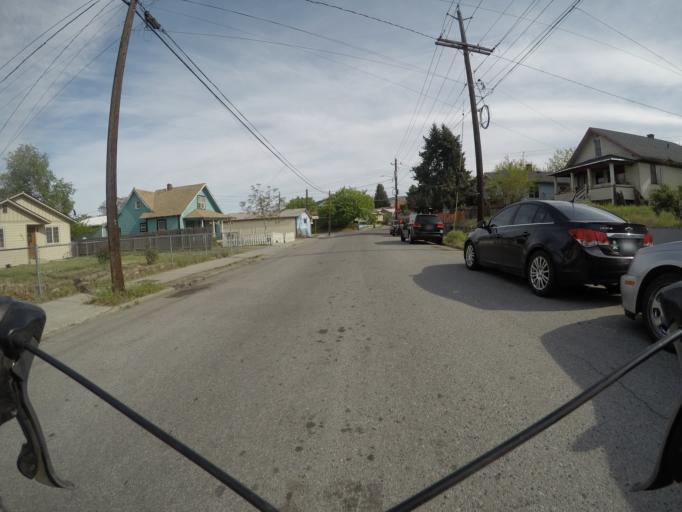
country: US
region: Washington
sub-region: Chelan County
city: Wenatchee
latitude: 47.4155
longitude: -120.3087
